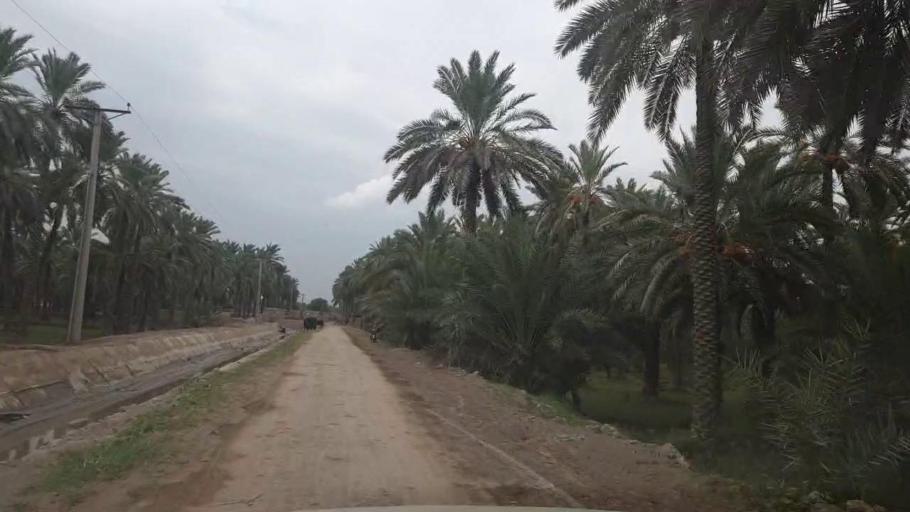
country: PK
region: Sindh
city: Khairpur
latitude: 27.6075
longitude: 68.8035
